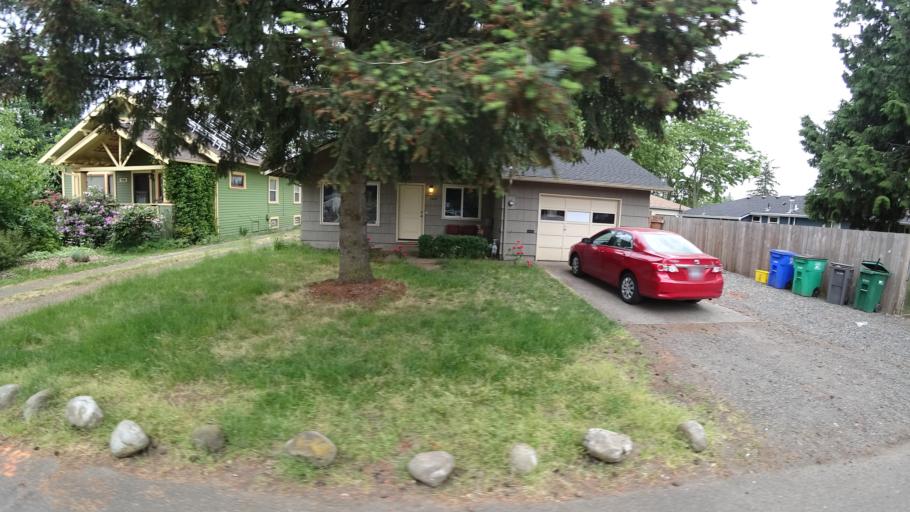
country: US
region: Oregon
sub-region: Multnomah County
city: Lents
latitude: 45.4720
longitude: -122.5825
